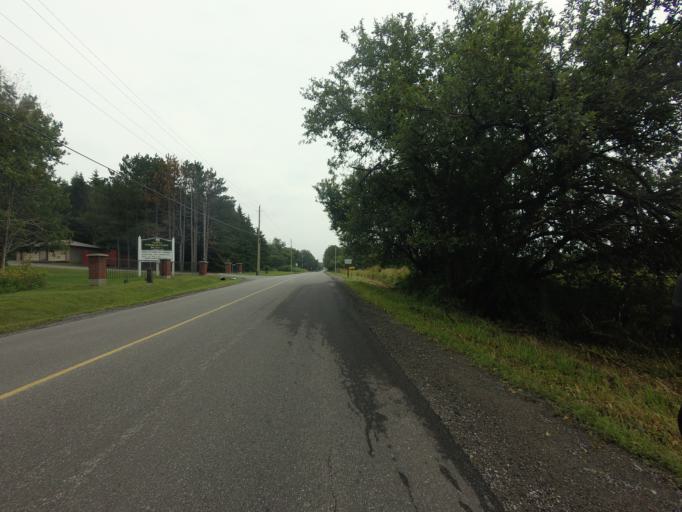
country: CA
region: Ontario
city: Bells Corners
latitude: 45.3404
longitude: -76.0042
